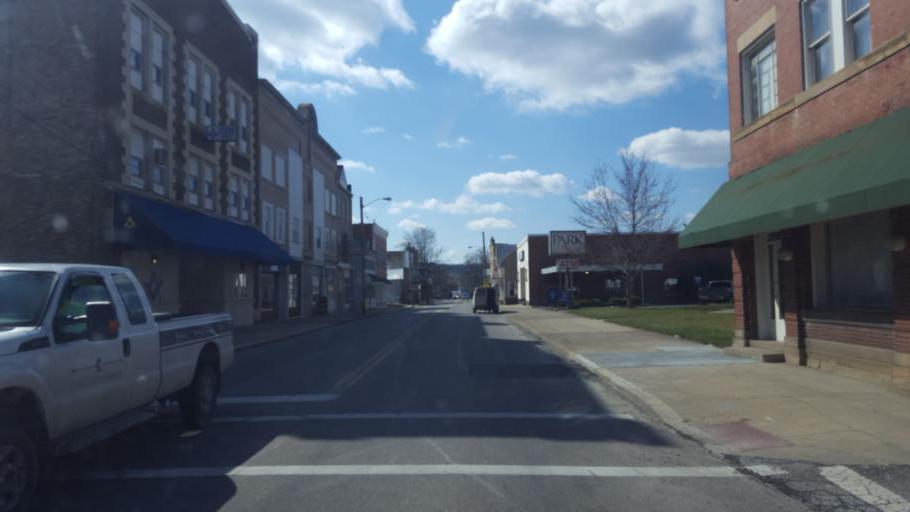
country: US
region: Ohio
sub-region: Licking County
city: Utica
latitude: 40.2345
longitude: -82.4527
